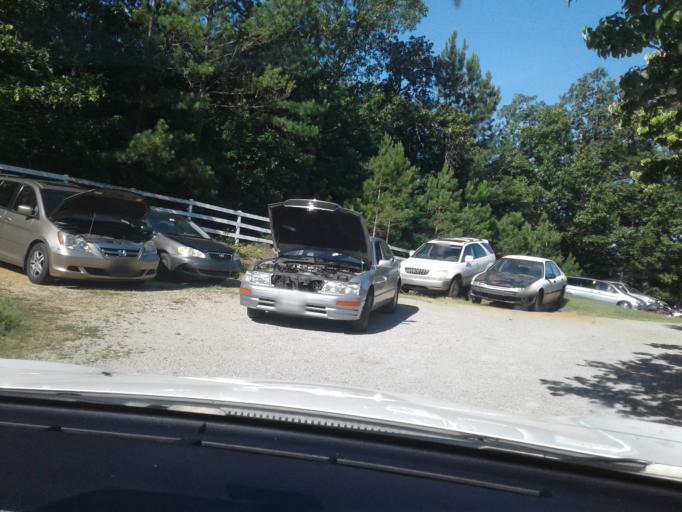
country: US
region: North Carolina
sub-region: Harnett County
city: Lillington
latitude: 35.4688
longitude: -78.8674
